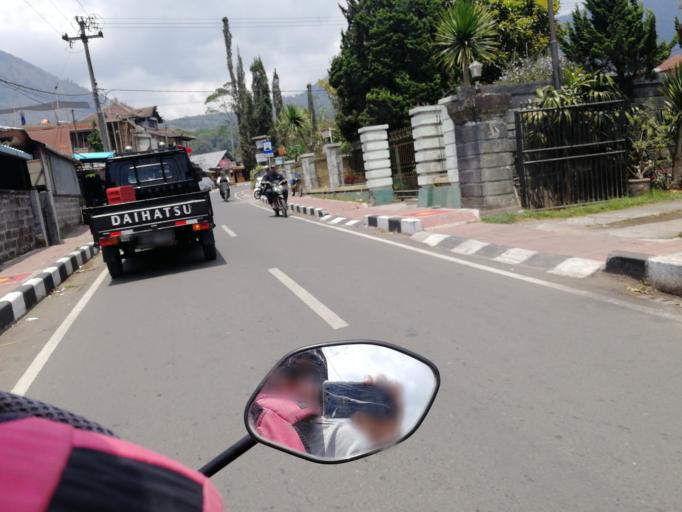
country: ID
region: Bali
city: Munduk
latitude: -8.2841
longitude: 115.1604
